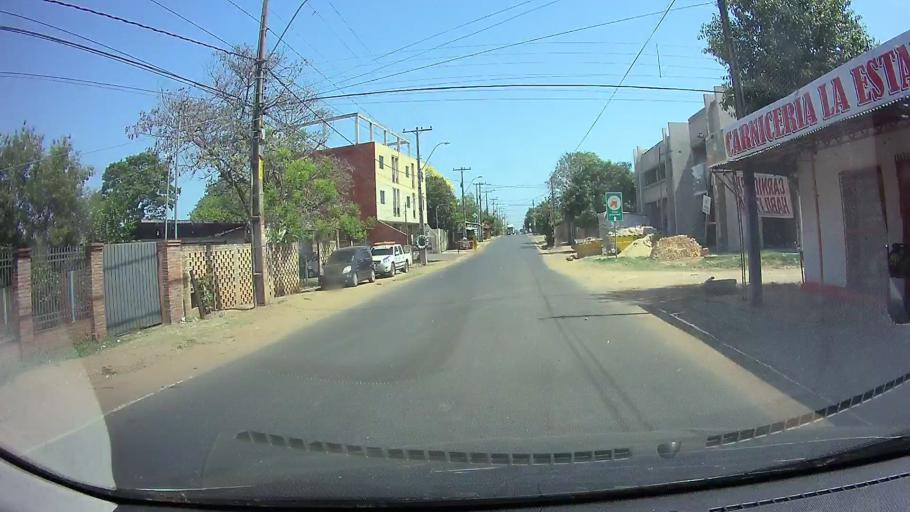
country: PY
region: Central
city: Limpio
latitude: -25.2079
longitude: -57.5165
